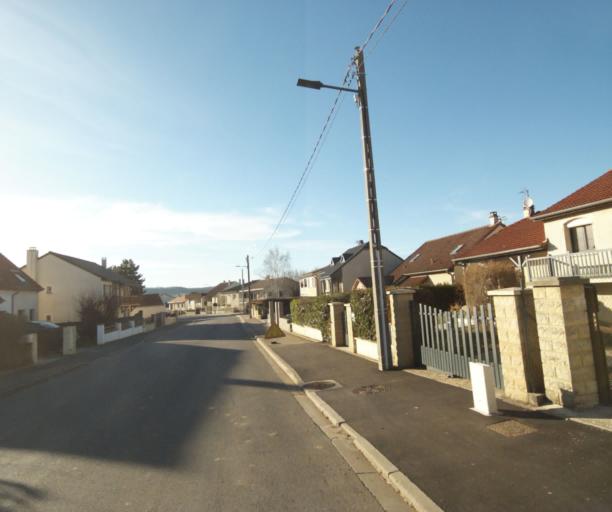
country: FR
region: Lorraine
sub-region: Departement de Meurthe-et-Moselle
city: Seichamps
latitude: 48.7160
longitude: 6.2739
